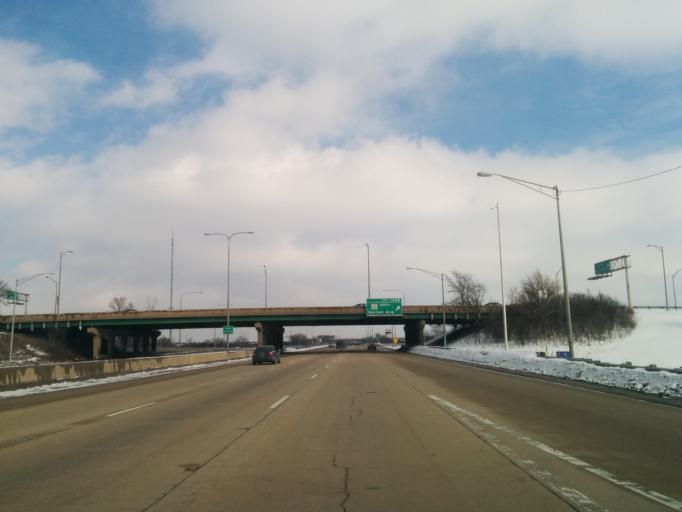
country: US
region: Illinois
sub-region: Cook County
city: Tinley Park
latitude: 41.5510
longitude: -87.7940
